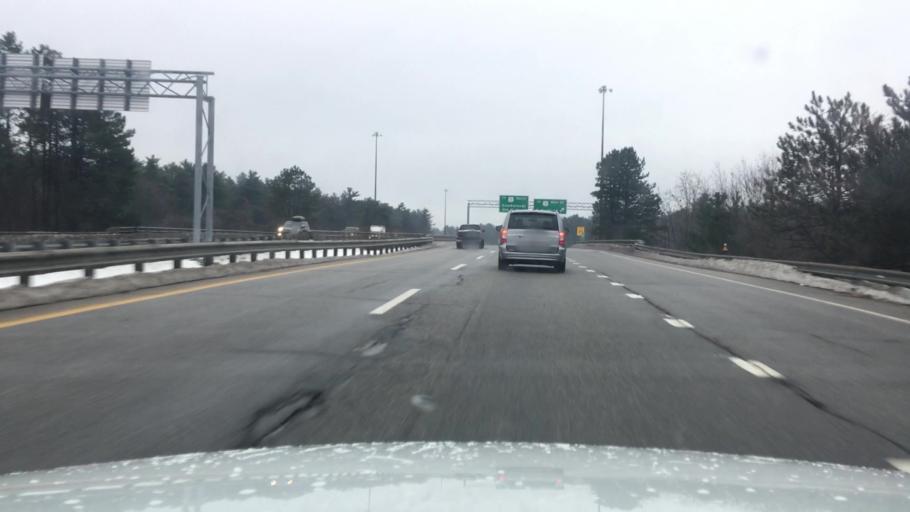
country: US
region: Maine
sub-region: Cumberland County
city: South Portland Gardens
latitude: 43.6247
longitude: -70.3195
